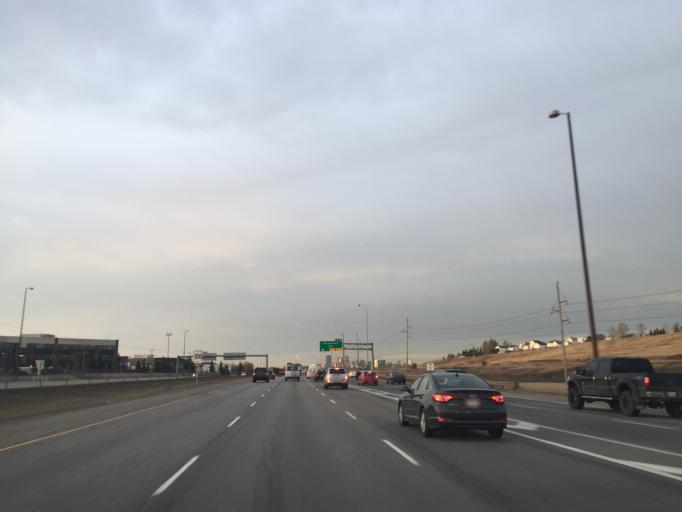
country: CA
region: Alberta
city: Calgary
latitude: 51.1217
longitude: -114.0462
